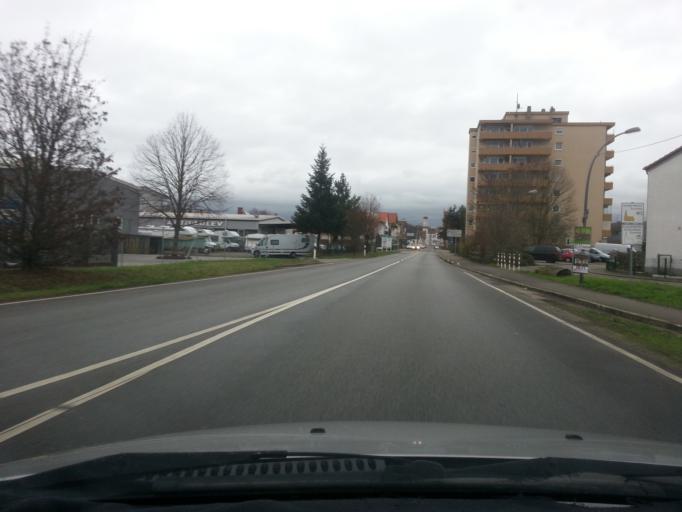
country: DE
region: Hesse
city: Lorsch
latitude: 49.5987
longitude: 8.5806
